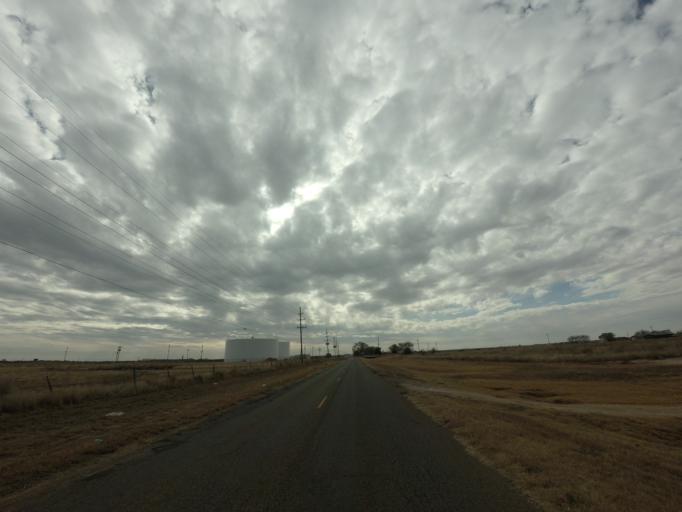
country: US
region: New Mexico
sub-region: Curry County
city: Clovis
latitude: 34.3925
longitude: -103.2319
